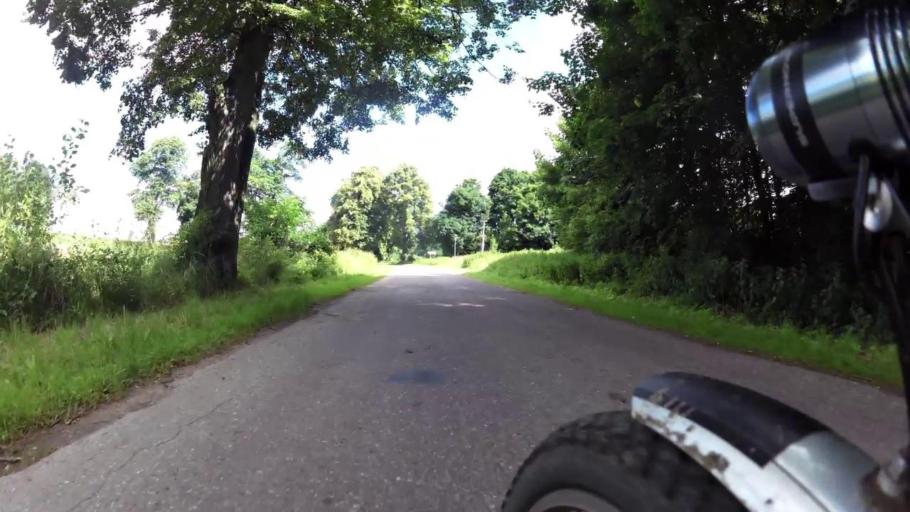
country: PL
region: West Pomeranian Voivodeship
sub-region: Powiat swidwinski
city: Rabino
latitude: 53.8147
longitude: 15.8914
